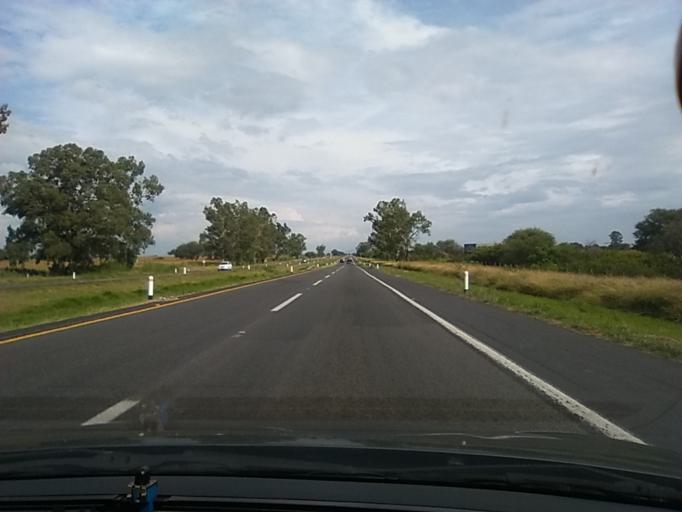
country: MX
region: Jalisco
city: La Barca
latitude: 20.3450
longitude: -102.6206
